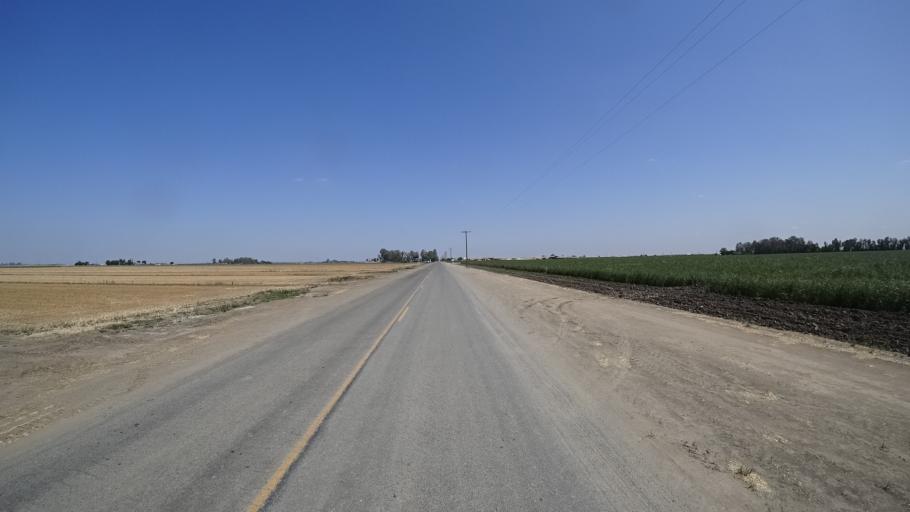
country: US
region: California
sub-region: Kings County
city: Home Garden
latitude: 36.2116
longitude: -119.6279
